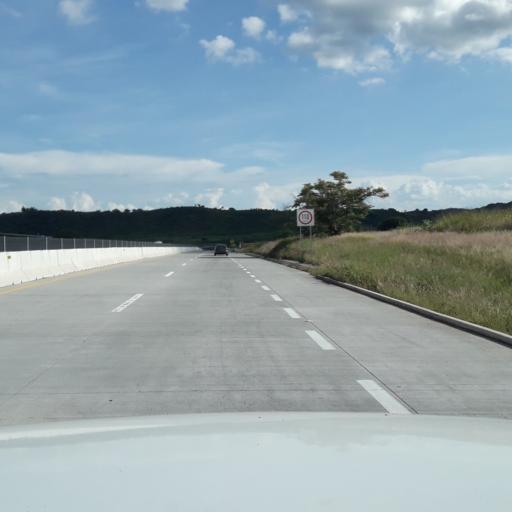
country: MX
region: Jalisco
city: Arenal
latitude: 20.7835
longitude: -103.7136
